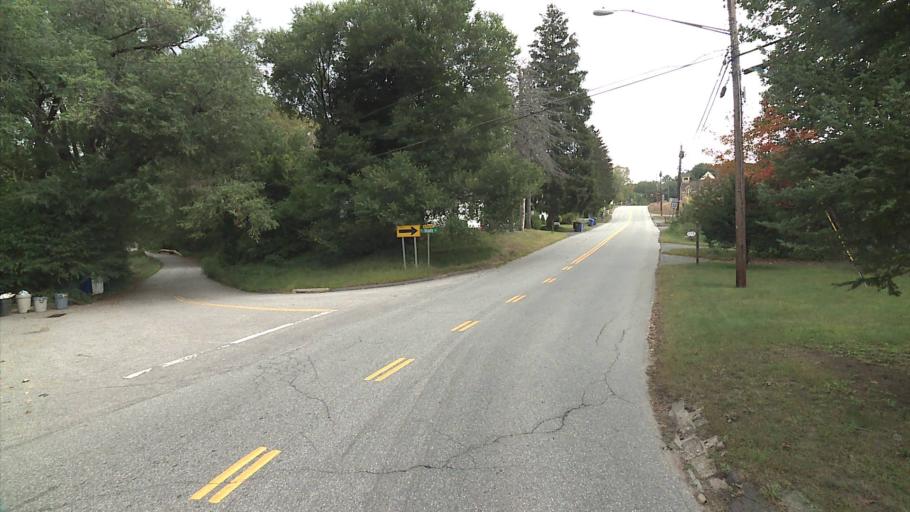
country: US
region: Connecticut
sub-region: Tolland County
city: South Coventry
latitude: 41.7856
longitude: -72.2787
